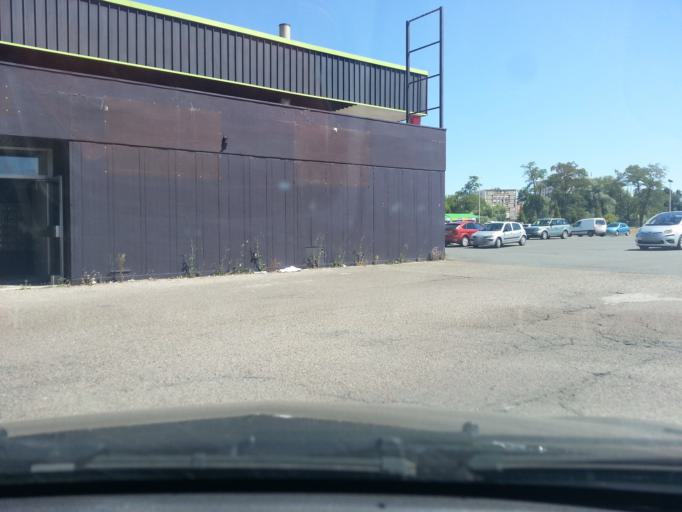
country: FR
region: Bourgogne
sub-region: Departement de Saone-et-Loire
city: Chatenoy-le-Royal
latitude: 46.7941
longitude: 4.8294
